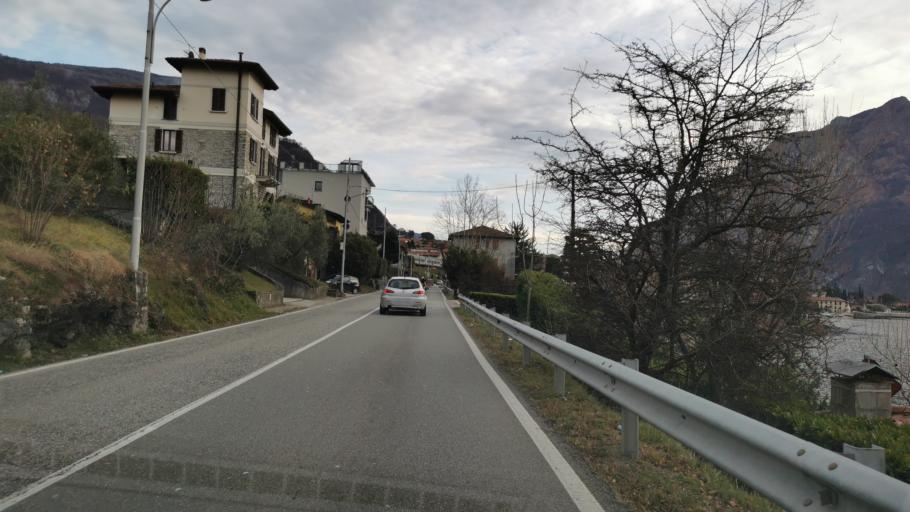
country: IT
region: Lombardy
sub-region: Provincia di Lecco
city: Abbadia Lariana
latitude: 45.9050
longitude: 9.3295
